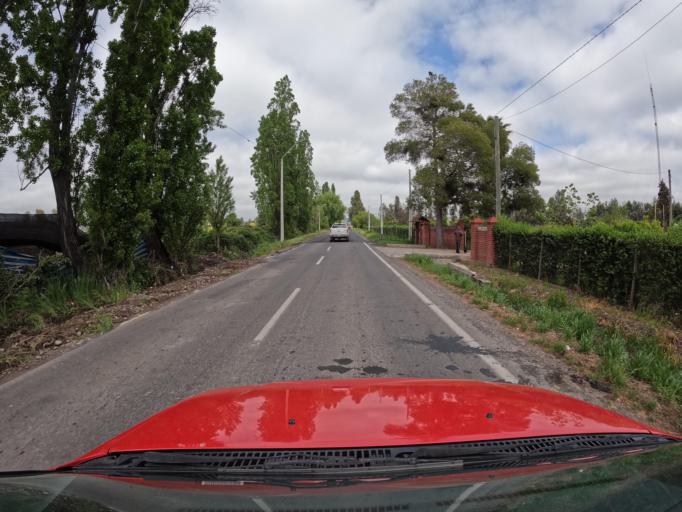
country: CL
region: O'Higgins
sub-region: Provincia de Colchagua
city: Santa Cruz
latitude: -34.6745
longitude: -71.3517
